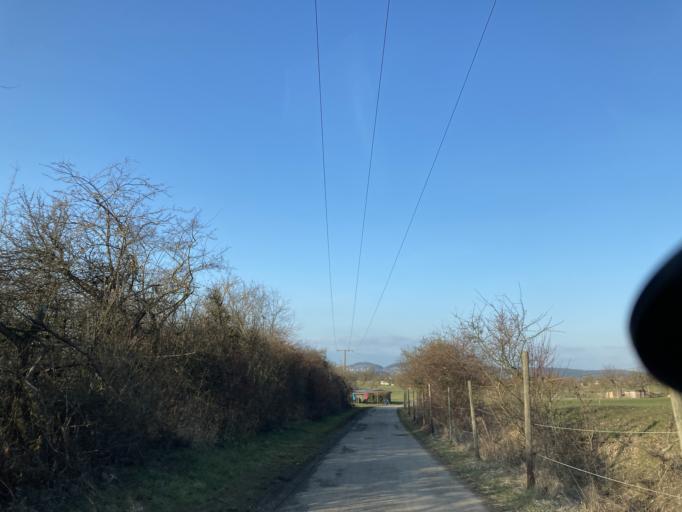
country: DE
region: Baden-Wuerttemberg
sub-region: Tuebingen Region
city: Hirrlingen
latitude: 48.4045
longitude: 8.8930
